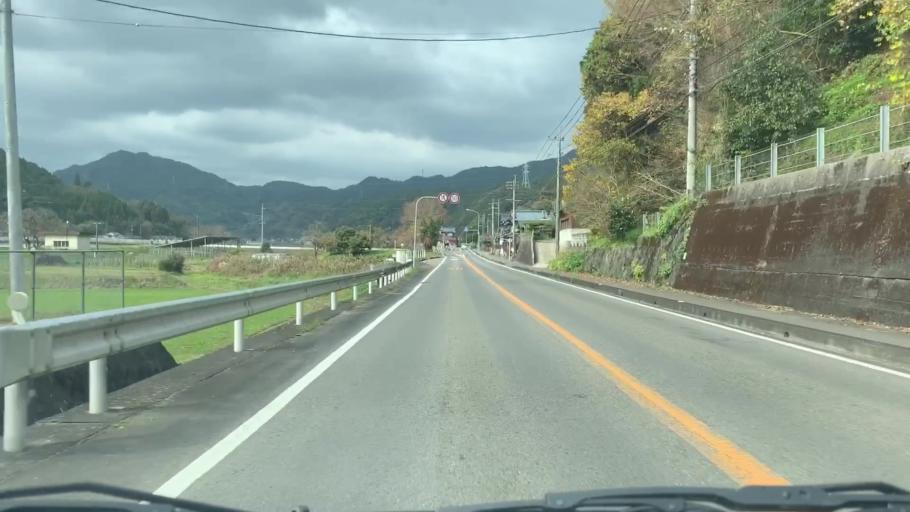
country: JP
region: Saga Prefecture
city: Ureshinomachi-shimojuku
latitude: 33.1297
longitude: 130.0333
